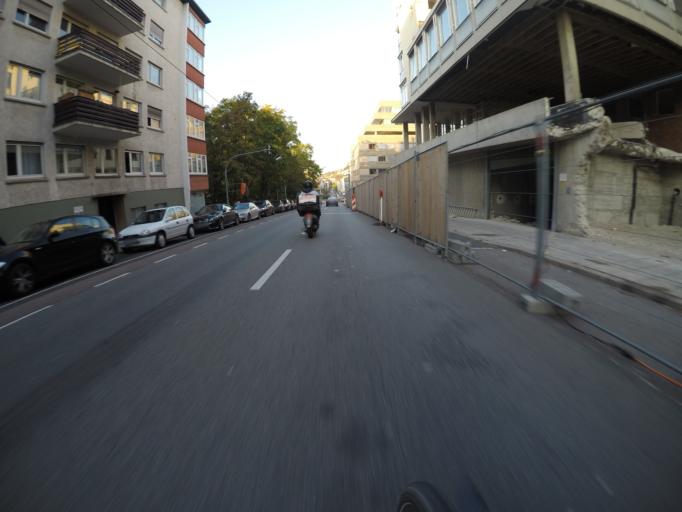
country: DE
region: Baden-Wuerttemberg
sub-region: Regierungsbezirk Stuttgart
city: Stuttgart
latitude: 48.7686
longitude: 9.1799
